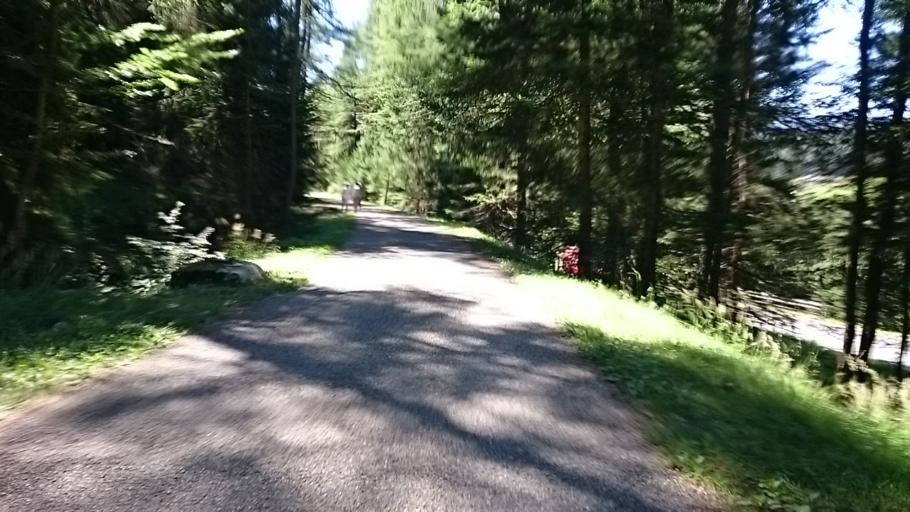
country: IT
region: Veneto
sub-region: Provincia di Belluno
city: Cortina d'Ampezzo
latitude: 46.5576
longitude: 12.1277
